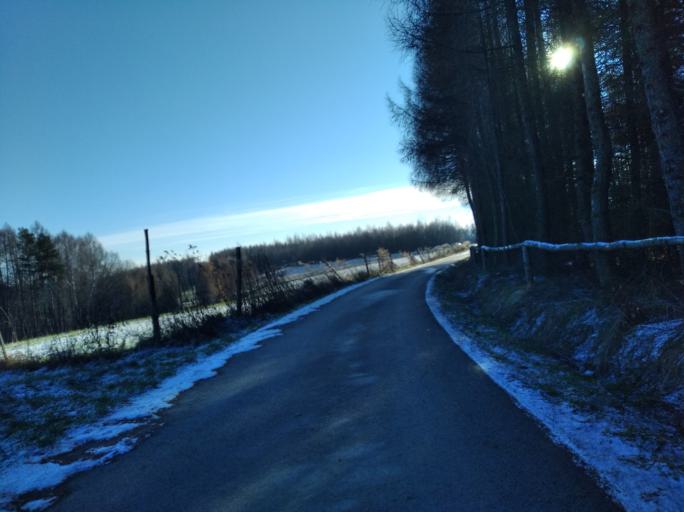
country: PL
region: Subcarpathian Voivodeship
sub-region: Powiat ropczycko-sedziszowski
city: Iwierzyce
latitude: 49.9632
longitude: 21.7512
